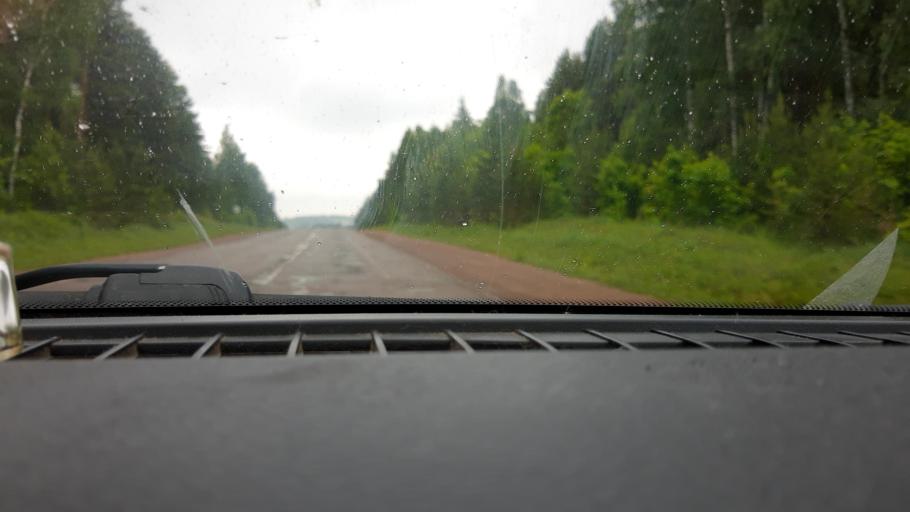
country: RU
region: Bashkortostan
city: Belebey
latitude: 54.1427
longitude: 54.0888
